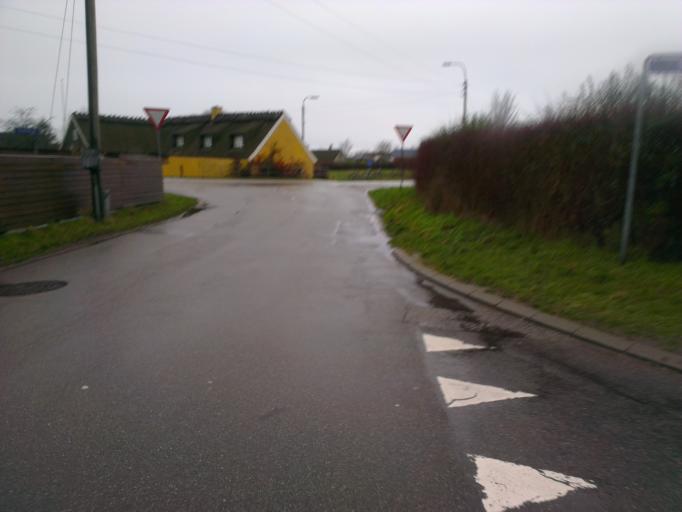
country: DK
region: Capital Region
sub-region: Frederikssund Kommune
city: Jaegerspris
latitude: 55.8367
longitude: 11.9890
